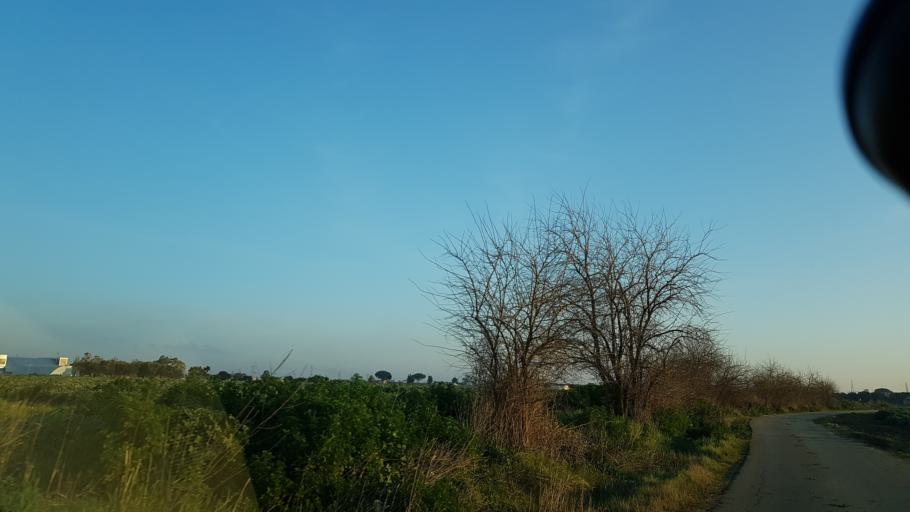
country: IT
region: Apulia
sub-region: Provincia di Brindisi
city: Brindisi
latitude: 40.6174
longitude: 17.9404
